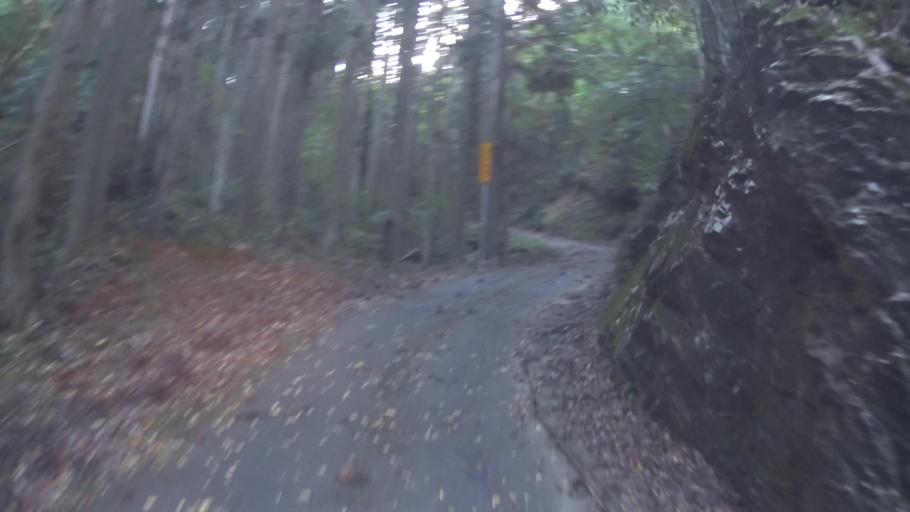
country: JP
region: Kyoto
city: Ayabe
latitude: 35.2697
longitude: 135.2483
